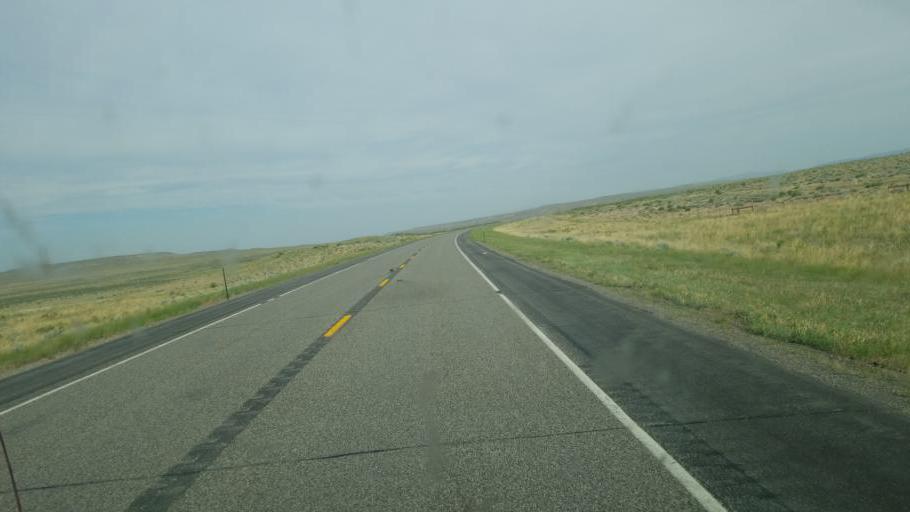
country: US
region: Wyoming
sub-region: Fremont County
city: Riverton
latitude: 43.1899
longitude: -107.9027
